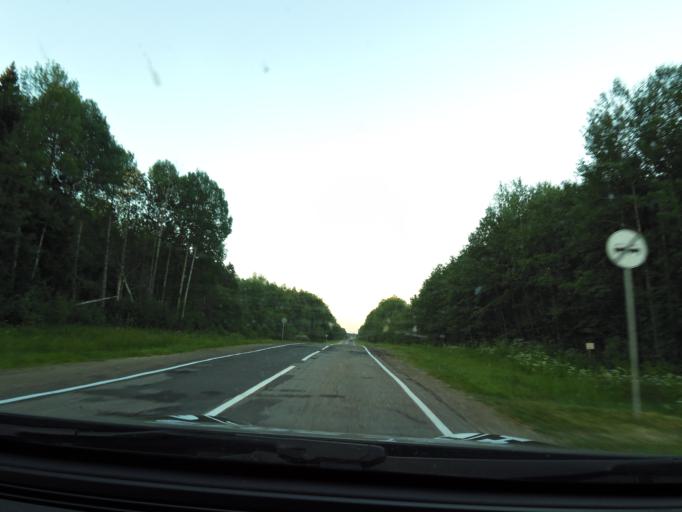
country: RU
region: Jaroslavl
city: Lyubim
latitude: 58.3573
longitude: 40.5847
